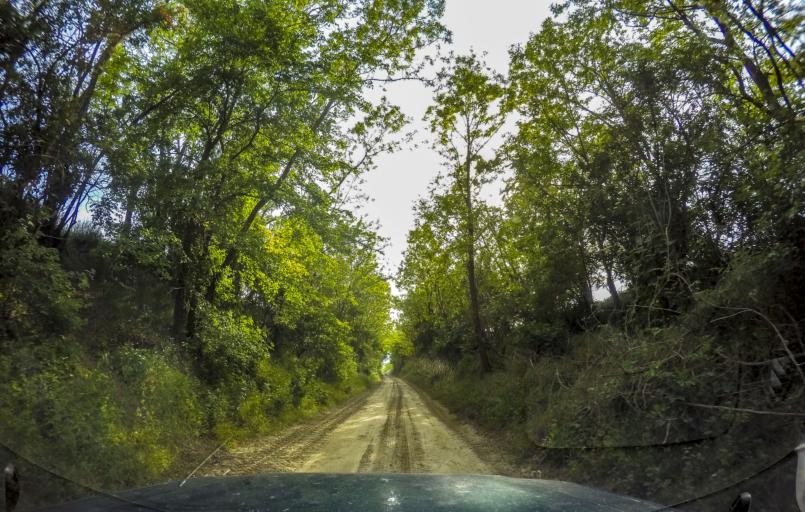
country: HU
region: Somogy
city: Karad
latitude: 46.7092
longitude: 17.8613
